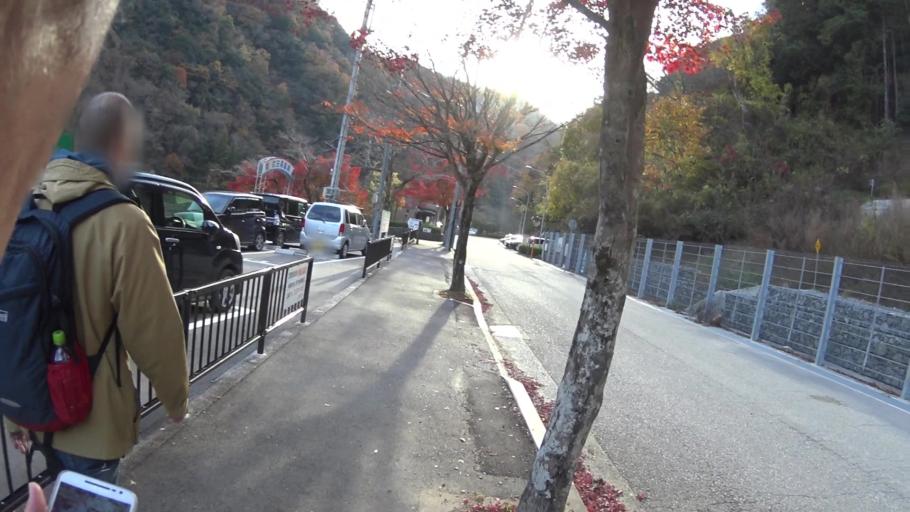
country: JP
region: Hyogo
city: Takarazuka
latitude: 34.8570
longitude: 135.3096
